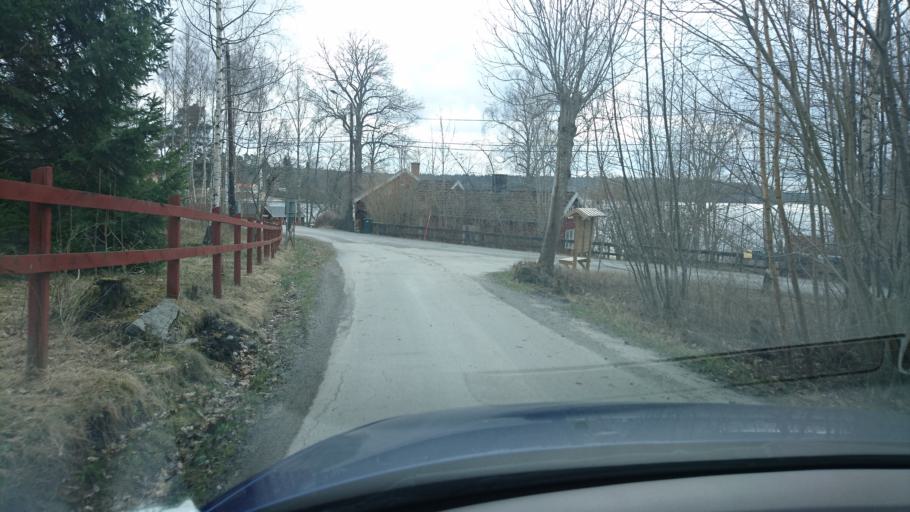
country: SE
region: Stockholm
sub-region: Norrtalje Kommun
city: Bjorko
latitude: 59.7841
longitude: 18.9488
